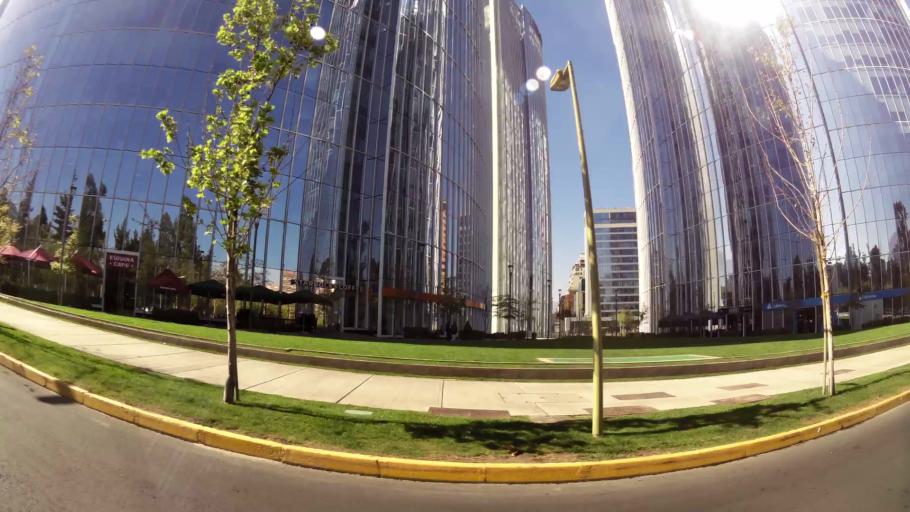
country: CL
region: Santiago Metropolitan
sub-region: Provincia de Santiago
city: Villa Presidente Frei, Nunoa, Santiago, Chile
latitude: -33.4112
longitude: -70.5796
